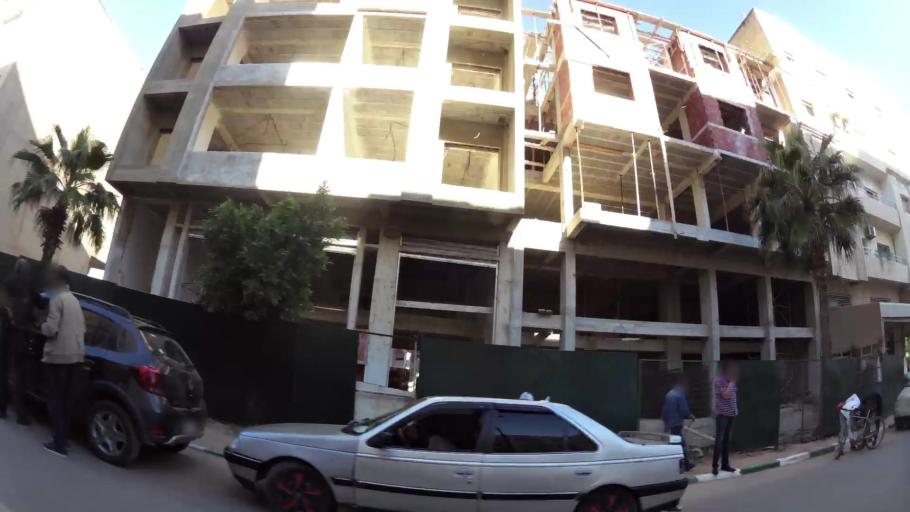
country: MA
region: Meknes-Tafilalet
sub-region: Meknes
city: Meknes
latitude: 33.8625
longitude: -5.5769
